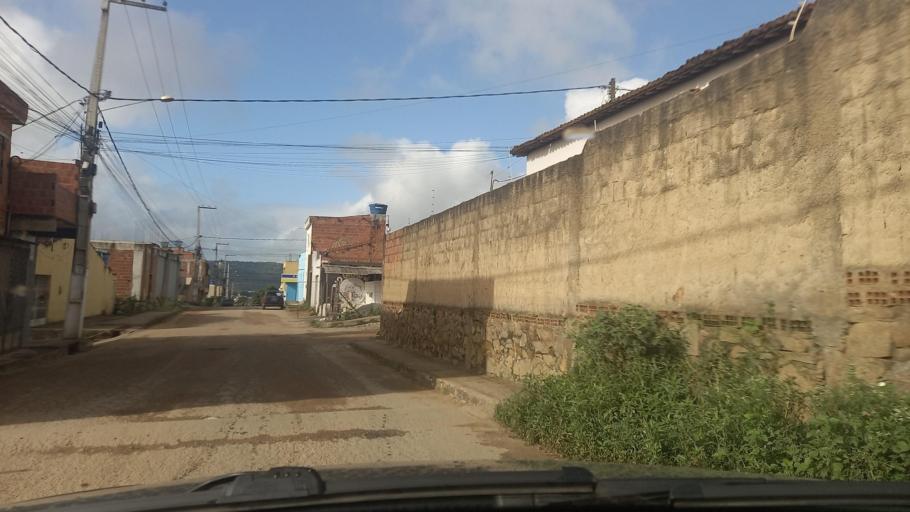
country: BR
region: Pernambuco
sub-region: Vitoria De Santo Antao
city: Vitoria de Santo Antao
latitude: -8.1127
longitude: -35.3079
